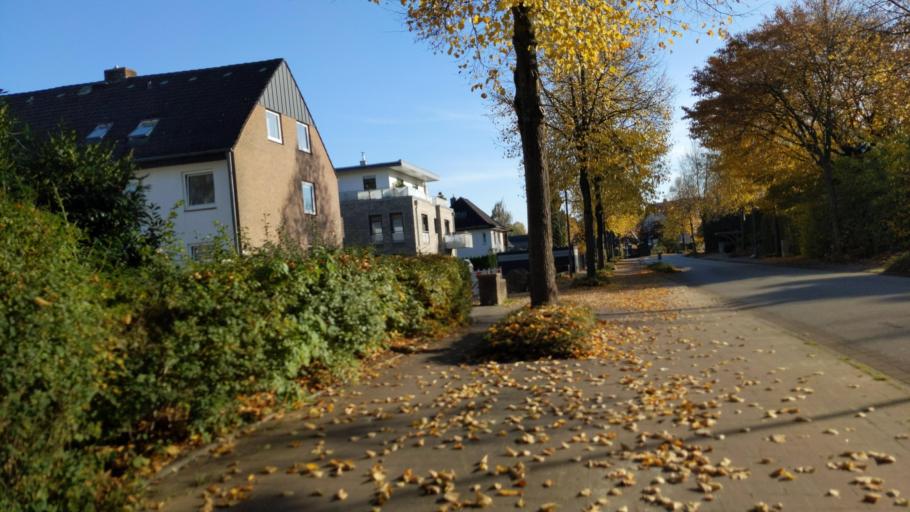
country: DE
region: Schleswig-Holstein
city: Eutin
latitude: 54.1475
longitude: 10.6095
